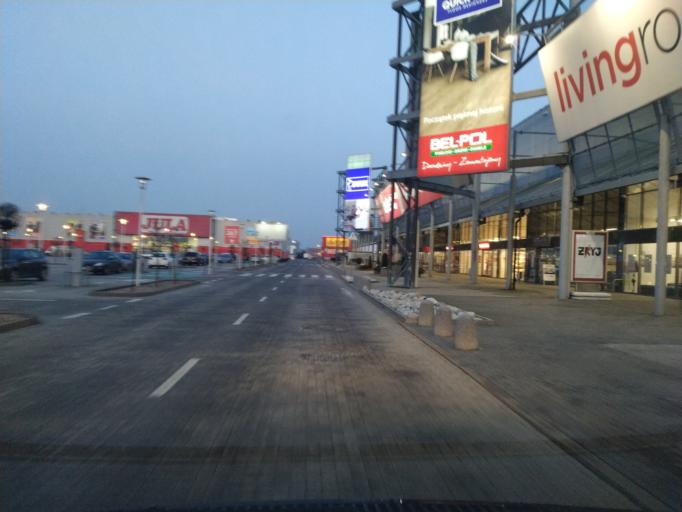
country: PL
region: Lower Silesian Voivodeship
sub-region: Powiat wroclawski
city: Bielany Wroclawskie
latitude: 51.0462
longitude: 16.9607
